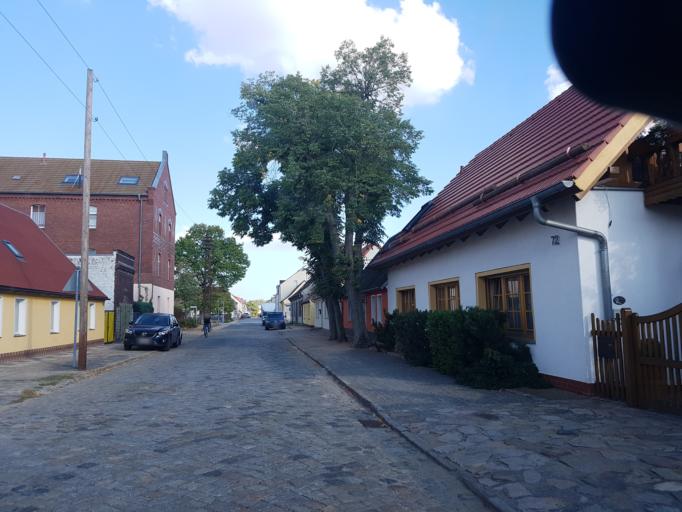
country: DE
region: Saxony-Anhalt
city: Wittenburg
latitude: 51.8646
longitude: 12.6074
